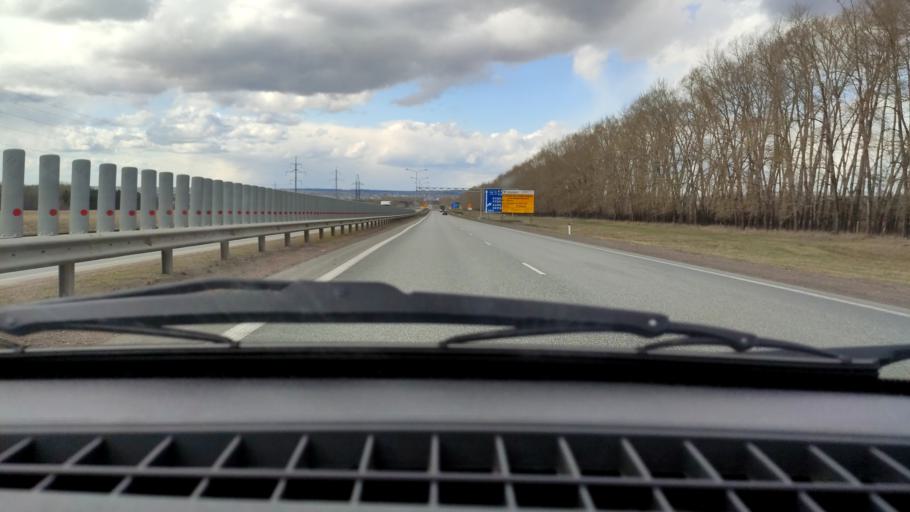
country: RU
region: Bashkortostan
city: Kushnarenkovo
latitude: 55.0519
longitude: 55.4388
